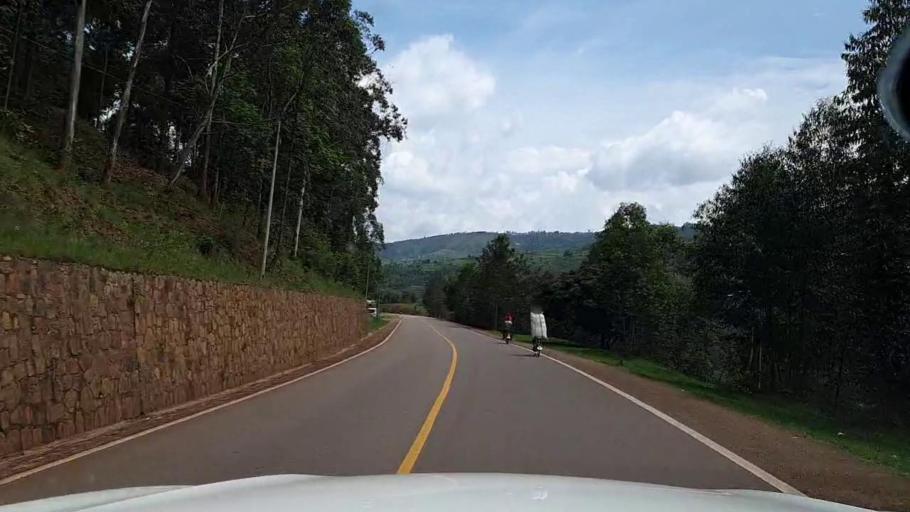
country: RW
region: Kigali
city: Kigali
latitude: -1.8584
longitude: 30.0949
